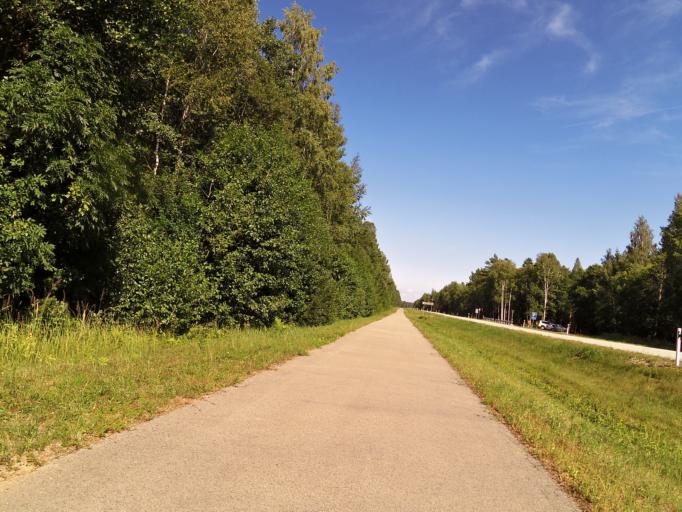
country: EE
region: Hiiumaa
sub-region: Kaerdla linn
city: Kardla
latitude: 59.0104
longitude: 22.6461
